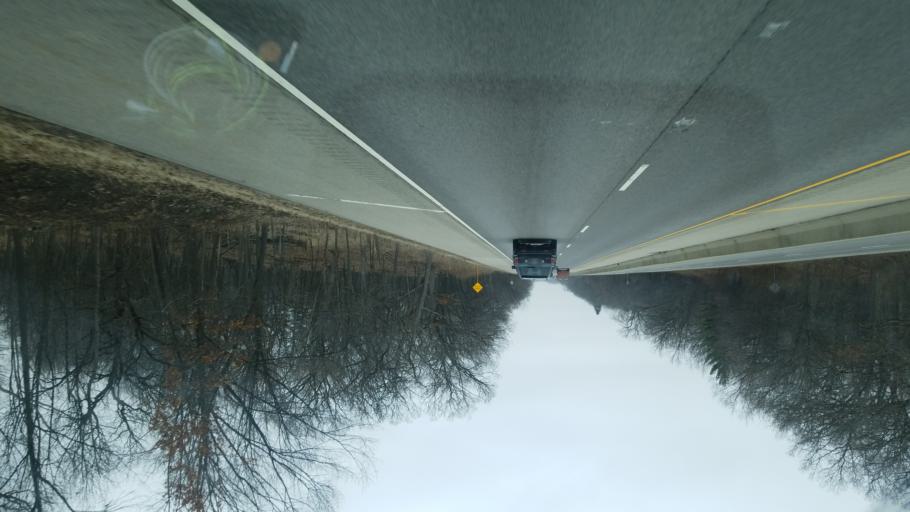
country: US
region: Illinois
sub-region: Lake County
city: Wadsworth
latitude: 42.4525
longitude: -87.9455
